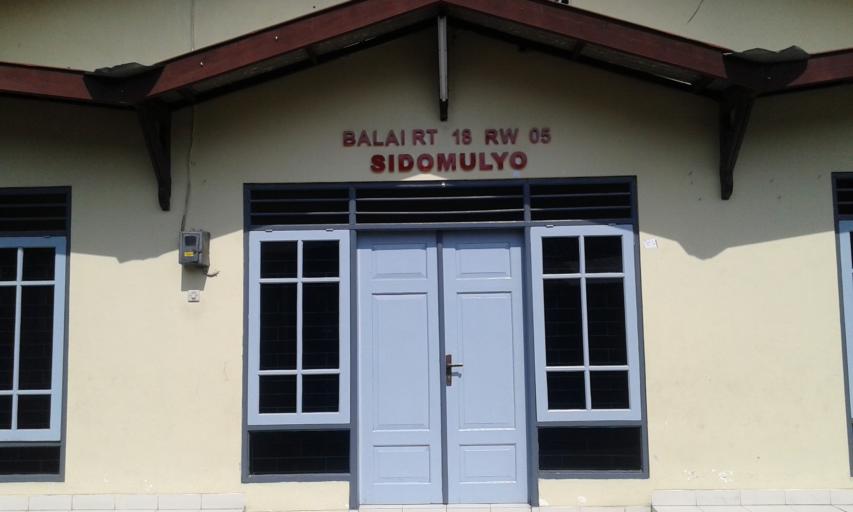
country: ID
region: Daerah Istimewa Yogyakarta
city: Yogyakarta
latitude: -7.7795
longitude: 110.3552
